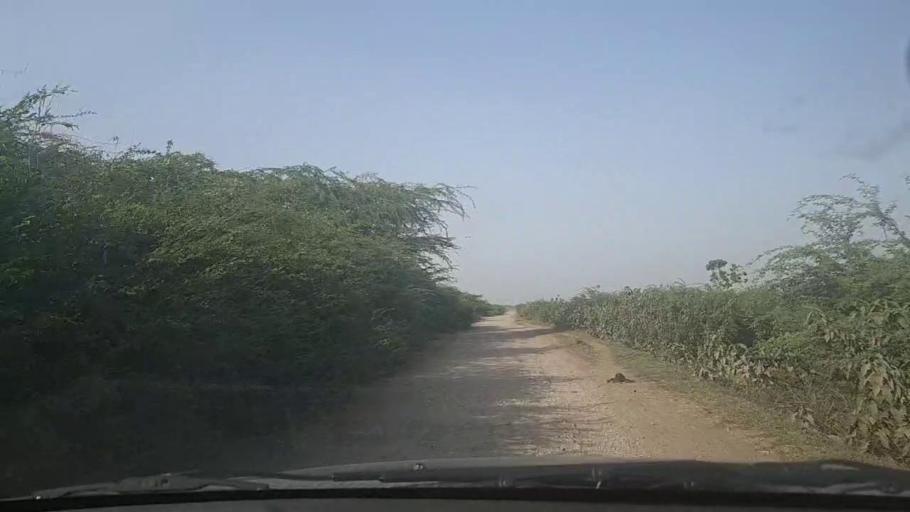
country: PK
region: Sindh
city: Keti Bandar
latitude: 24.2599
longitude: 67.5645
